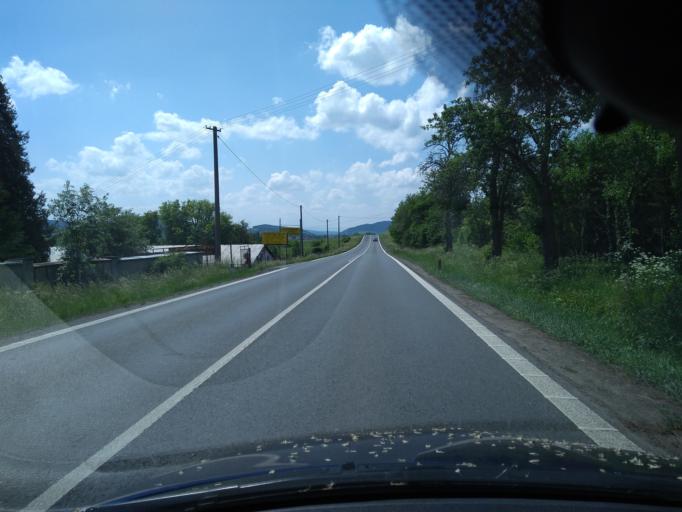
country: CZ
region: Plzensky
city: Prestice
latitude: 49.5666
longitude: 13.3253
